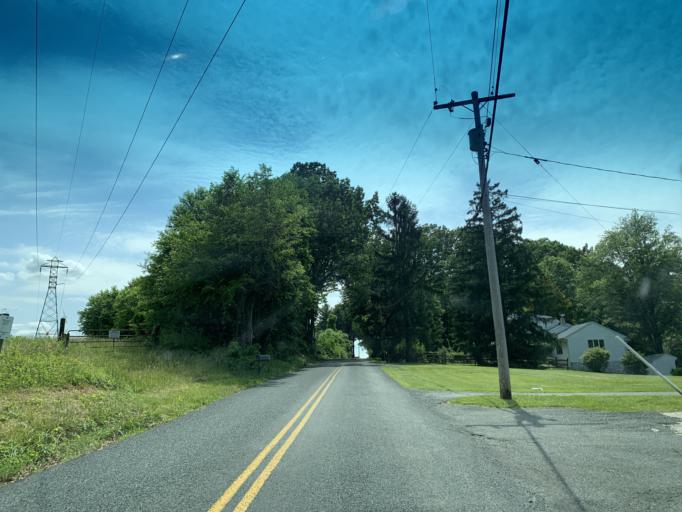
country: US
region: Maryland
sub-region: Harford County
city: Jarrettsville
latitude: 39.6458
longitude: -76.4438
